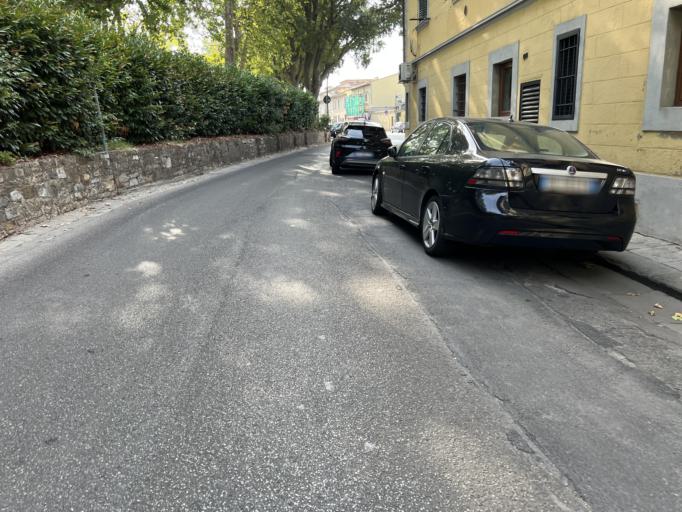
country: IT
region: Tuscany
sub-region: Province of Florence
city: Florence
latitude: 43.7731
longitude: 11.2370
